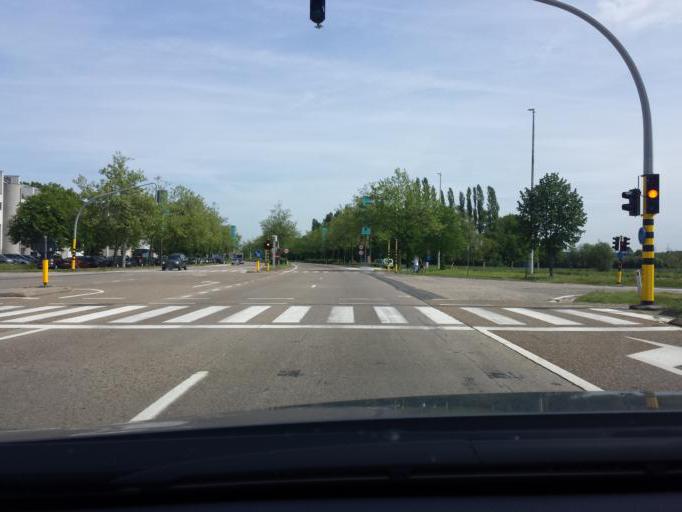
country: BE
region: Flanders
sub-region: Provincie Limburg
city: Hasselt
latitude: 50.9191
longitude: 5.3536
